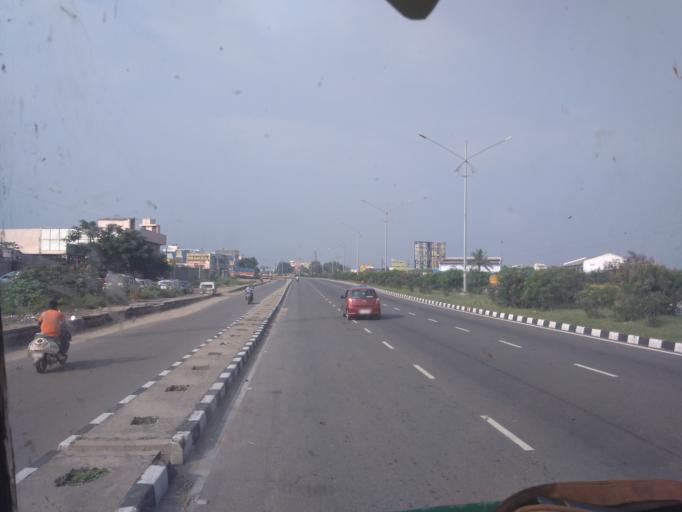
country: IN
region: Tamil Nadu
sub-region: Vellore
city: Vellore
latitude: 12.9249
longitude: 79.1149
